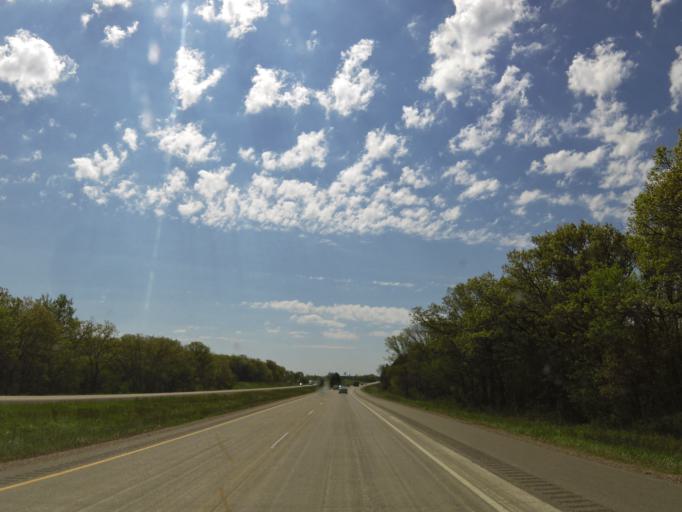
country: US
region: Wisconsin
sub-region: Eau Claire County
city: Fall Creek
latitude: 44.6772
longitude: -91.3250
